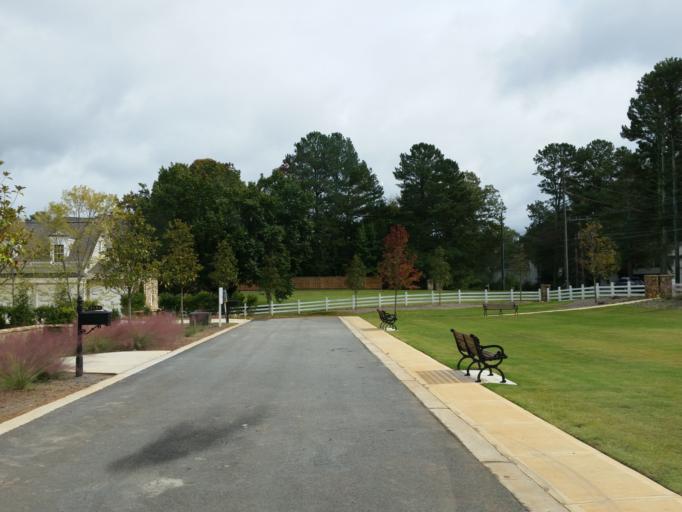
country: US
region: Georgia
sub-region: Fulton County
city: Roswell
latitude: 34.0072
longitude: -84.4581
